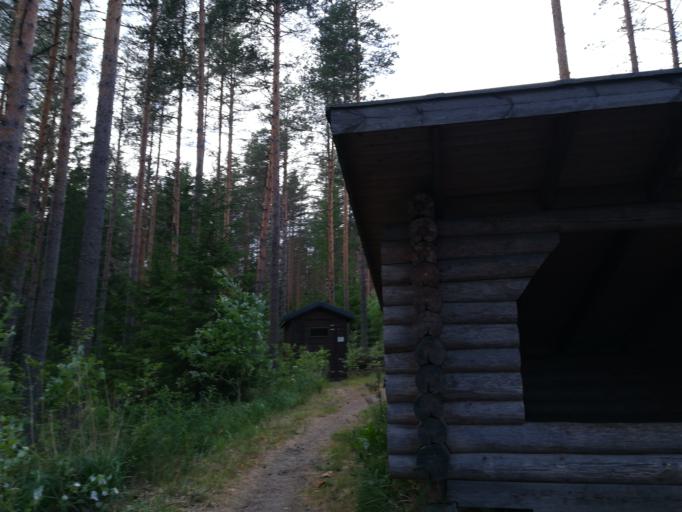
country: FI
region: South Karelia
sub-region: Lappeenranta
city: Savitaipale
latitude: 61.3091
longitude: 27.6330
